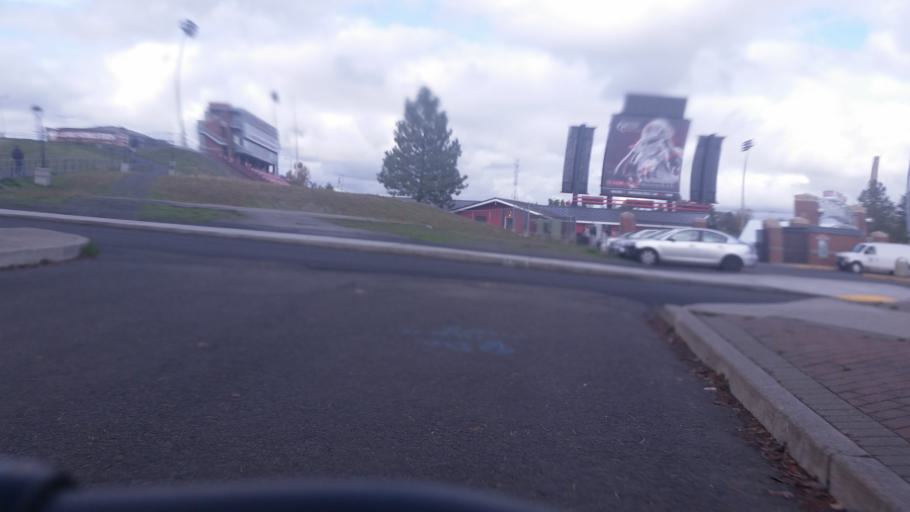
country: US
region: Washington
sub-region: Spokane County
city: Cheney
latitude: 47.4911
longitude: -117.5878
